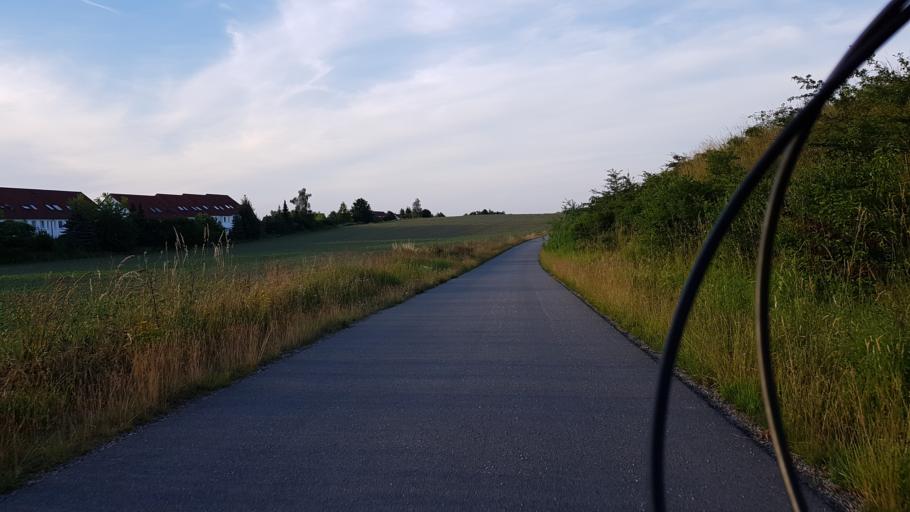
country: DE
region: Mecklenburg-Vorpommern
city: Lankow
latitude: 53.6507
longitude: 11.3460
